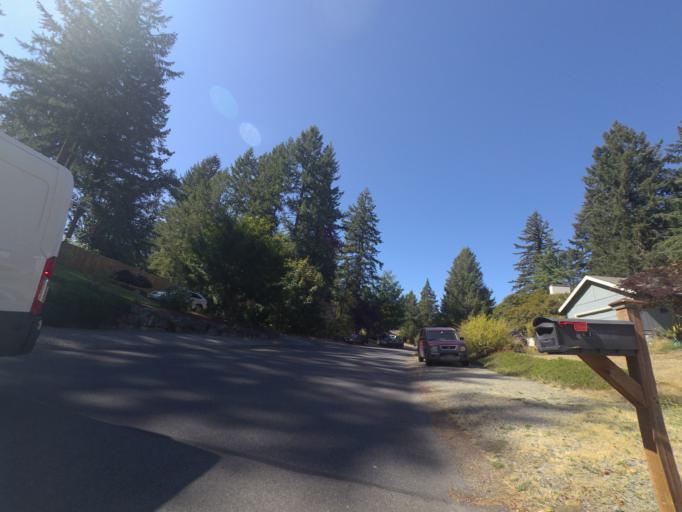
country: US
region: Washington
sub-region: Pierce County
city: Fircrest
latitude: 47.2161
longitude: -122.5196
